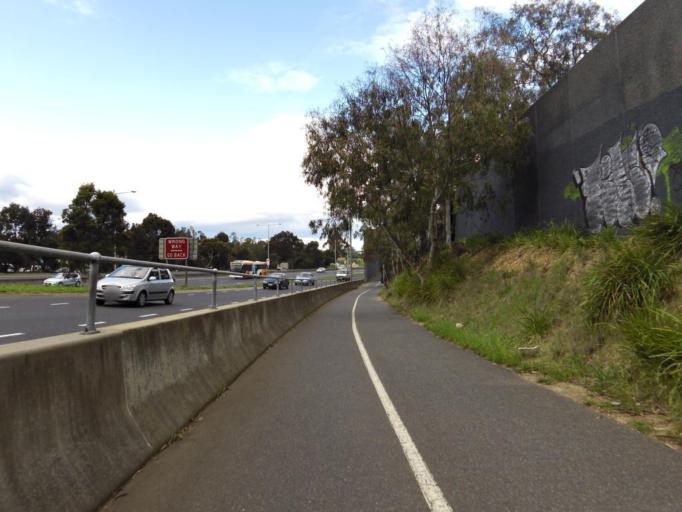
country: AU
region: Victoria
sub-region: Manningham
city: Bulleen
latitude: -37.7803
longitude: 145.0804
